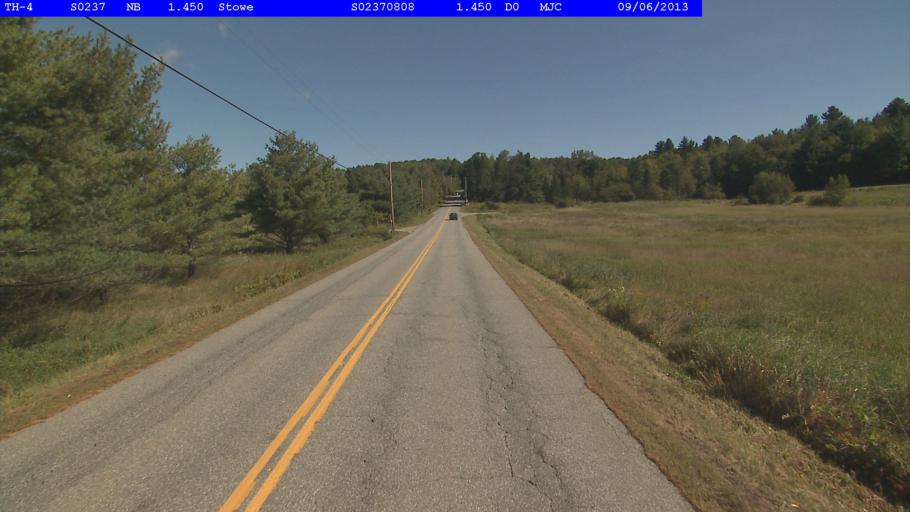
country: US
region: Vermont
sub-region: Lamoille County
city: Morristown
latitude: 44.5011
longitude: -72.6556
